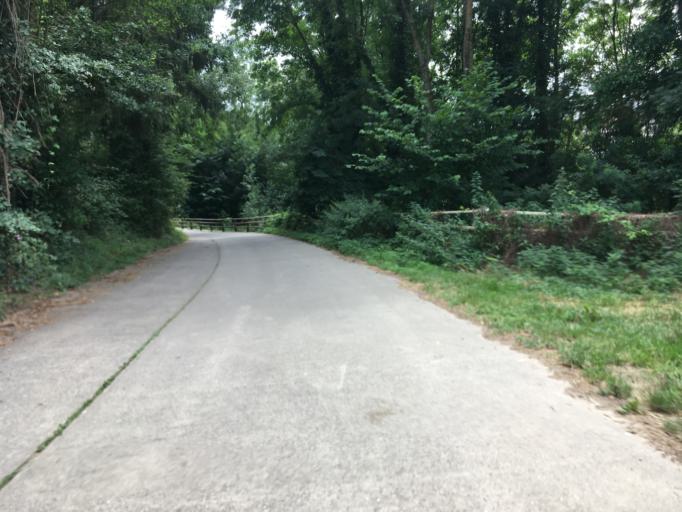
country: CH
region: Fribourg
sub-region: Broye District
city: Estavayer-le-Lac
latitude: 46.8781
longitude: 6.8899
